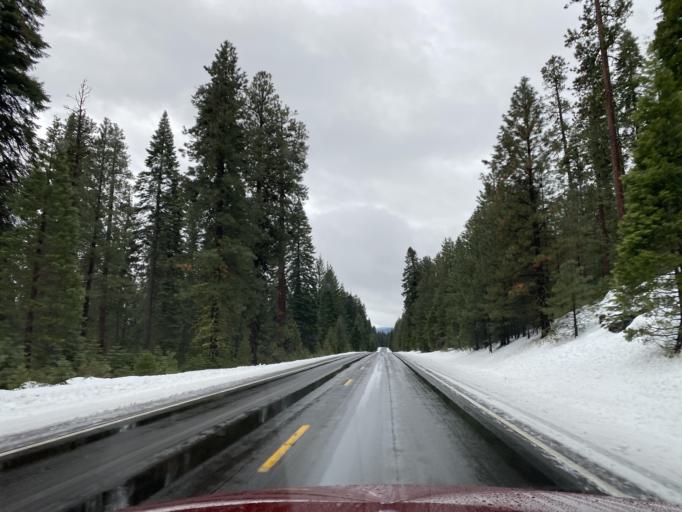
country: US
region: Oregon
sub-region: Klamath County
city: Klamath Falls
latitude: 42.5127
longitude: -122.0835
